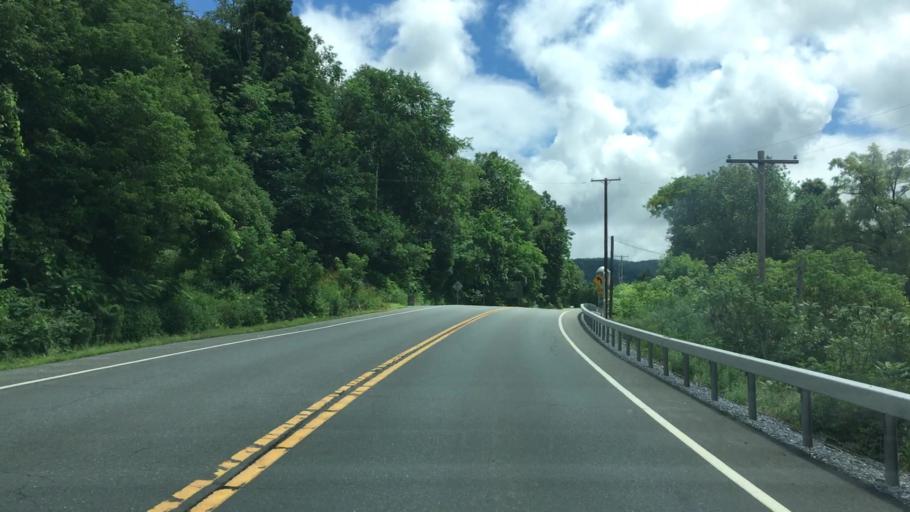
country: US
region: Vermont
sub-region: Bennington County
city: North Bennington
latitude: 42.8766
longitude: -73.2789
